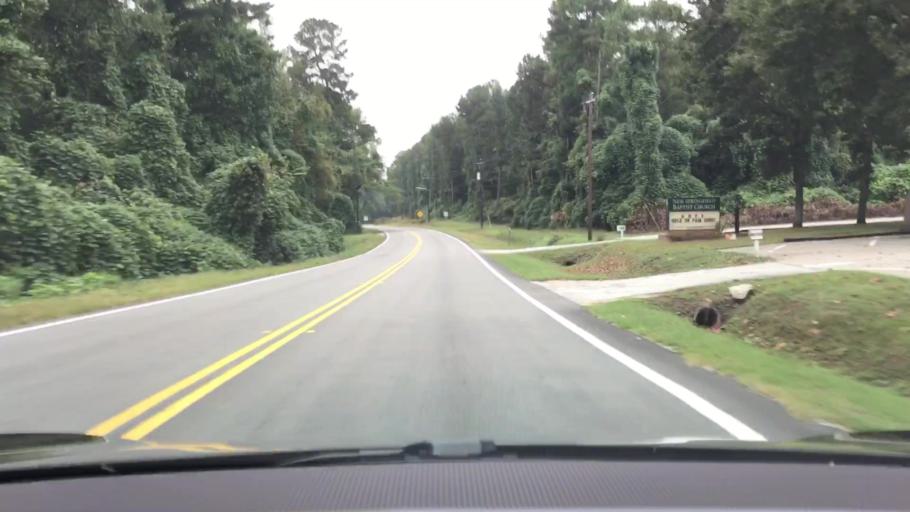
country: US
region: Georgia
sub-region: Greene County
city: Union Point
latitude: 33.5386
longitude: -83.0868
